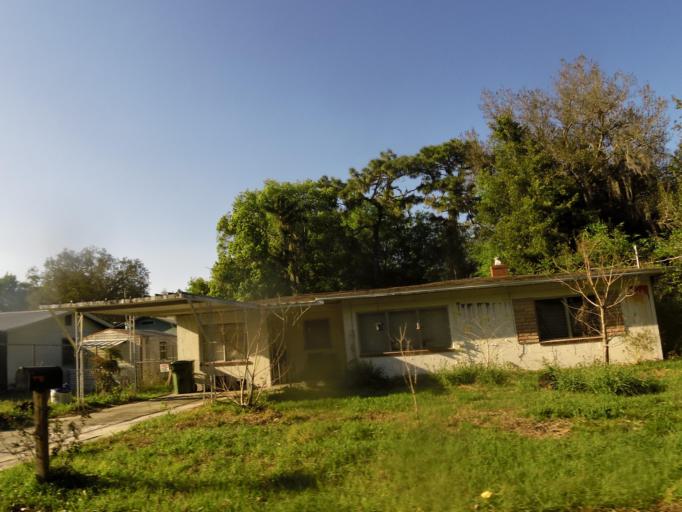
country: US
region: Florida
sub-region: Putnam County
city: Palatka
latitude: 29.6454
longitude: -81.6557
